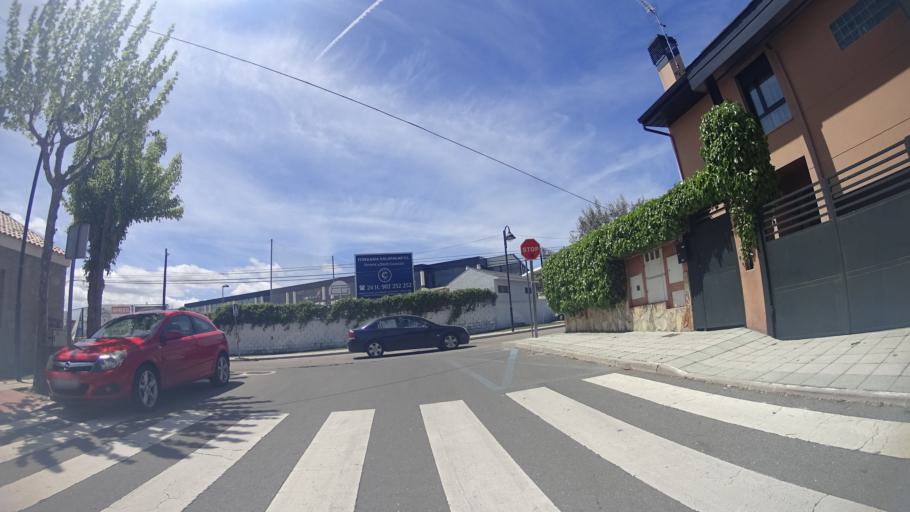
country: ES
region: Madrid
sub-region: Provincia de Madrid
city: Galapagar
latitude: 40.5830
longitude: -4.0094
